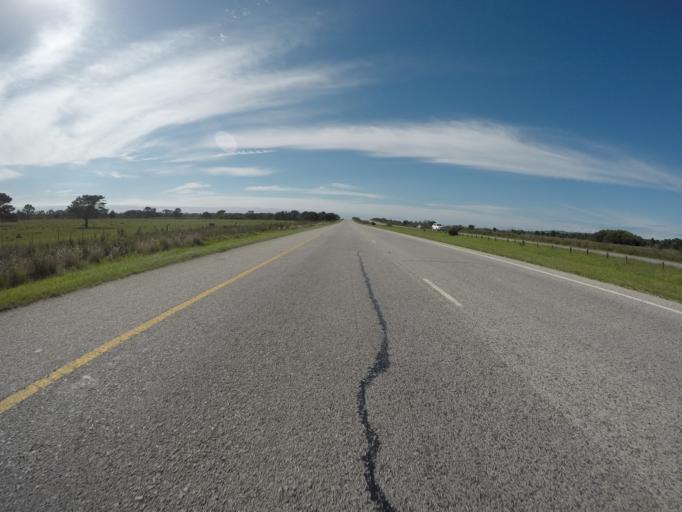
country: ZA
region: Eastern Cape
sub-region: Nelson Mandela Bay Metropolitan Municipality
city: Port Elizabeth
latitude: -33.9496
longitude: 25.4362
